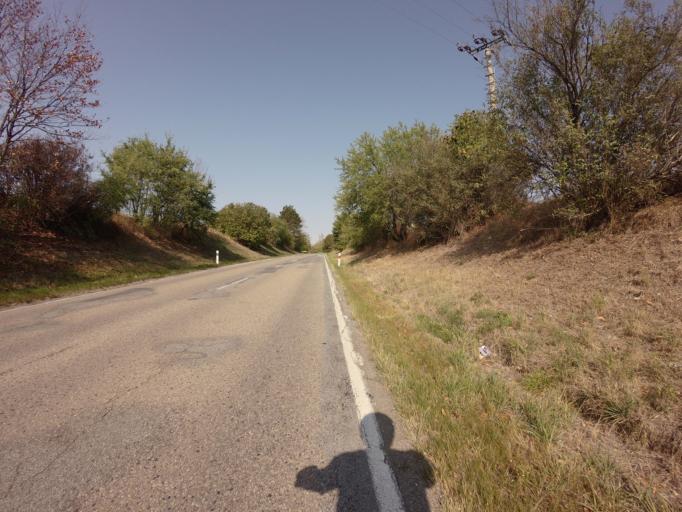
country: CZ
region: Central Bohemia
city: Tynec nad Sazavou
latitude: 49.8255
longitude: 14.6207
